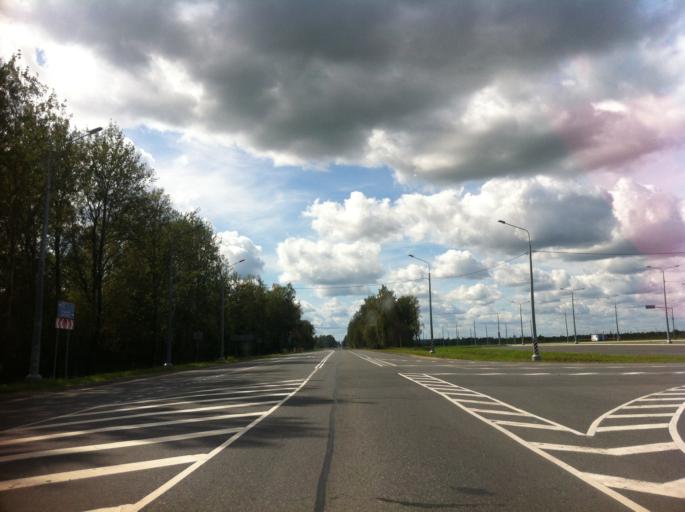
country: RU
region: Pskov
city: Pskov
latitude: 57.7743
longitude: 28.1408
